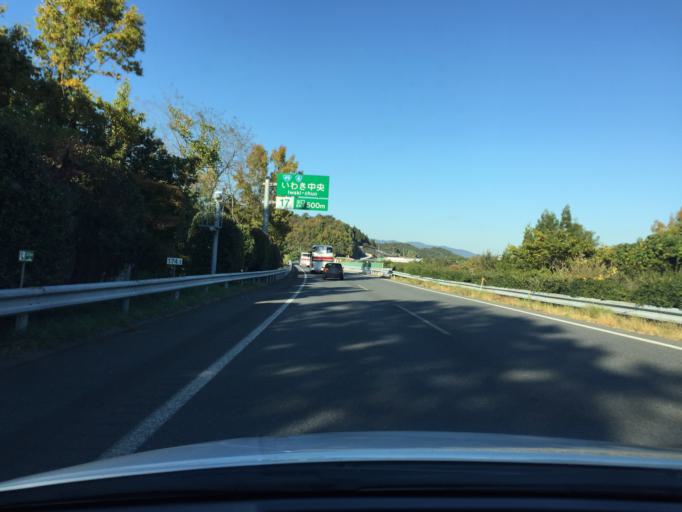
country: JP
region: Fukushima
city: Iwaki
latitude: 37.0598
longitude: 140.8315
